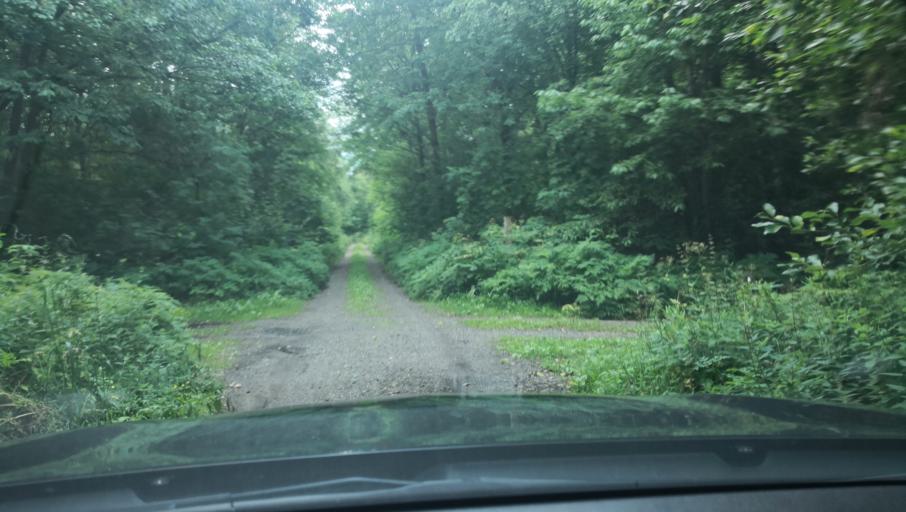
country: SE
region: Skane
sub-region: Simrishamns Kommun
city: Kivik
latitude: 55.6285
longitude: 14.1258
